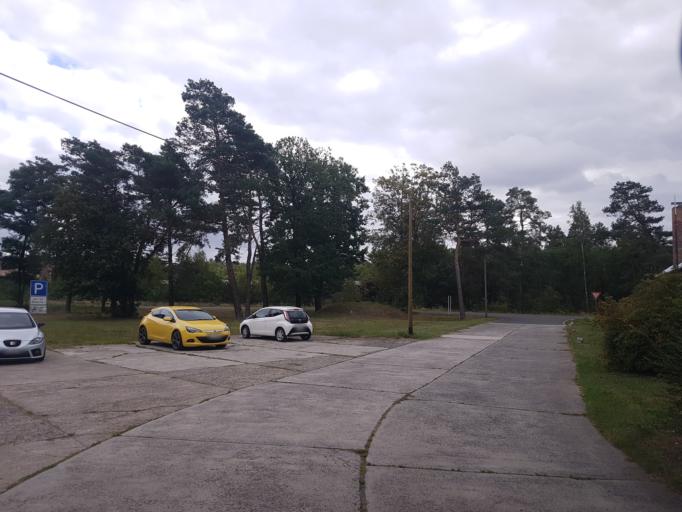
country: DE
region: Brandenburg
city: Finsterwalde
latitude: 51.6029
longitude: 13.7448
